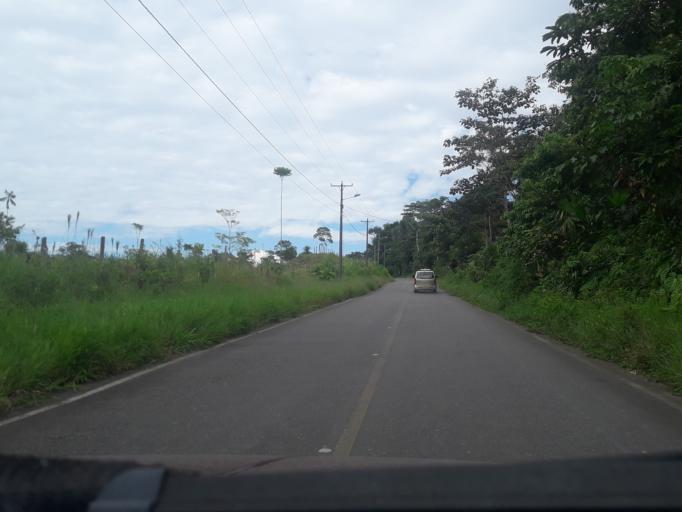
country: EC
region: Napo
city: Tena
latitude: -1.0339
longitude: -77.8893
